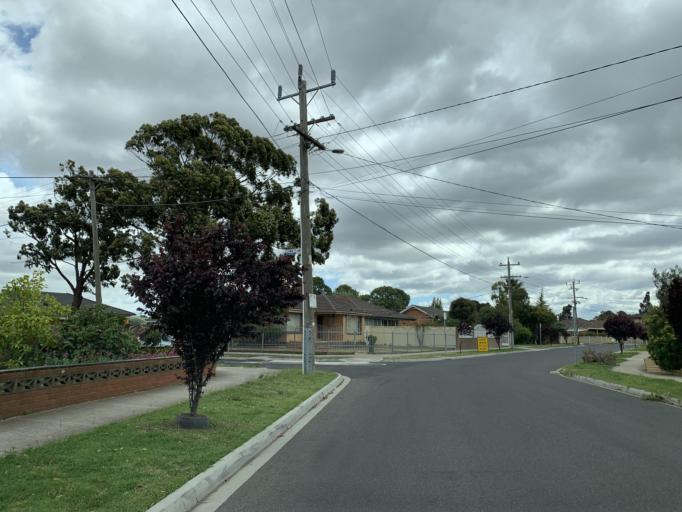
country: AU
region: Victoria
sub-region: Brimbank
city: St Albans
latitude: -37.7594
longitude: 144.8083
